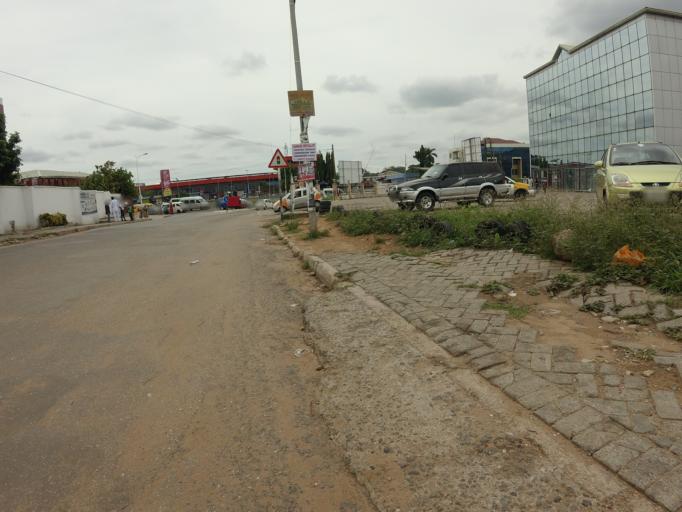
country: GH
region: Greater Accra
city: Dome
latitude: 5.6240
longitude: -0.2342
